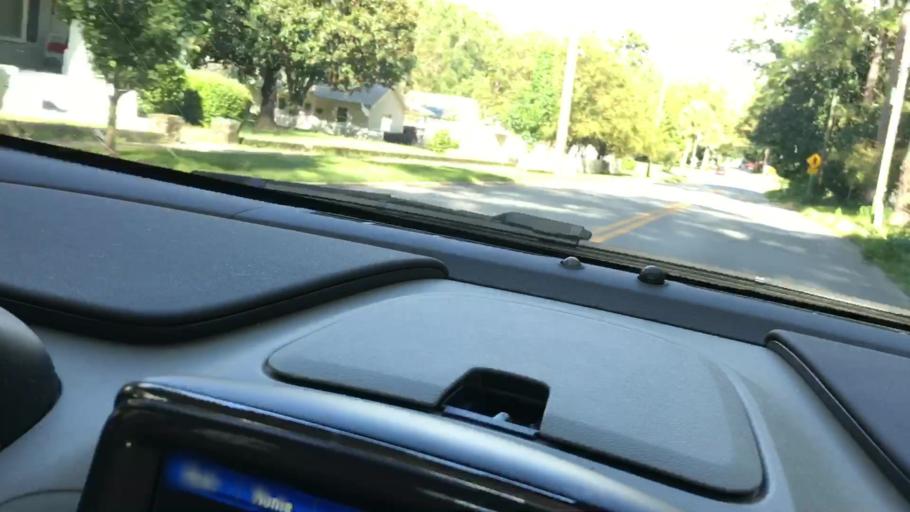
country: US
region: Florida
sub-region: Washington County
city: Chipley
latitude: 30.7862
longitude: -85.5417
